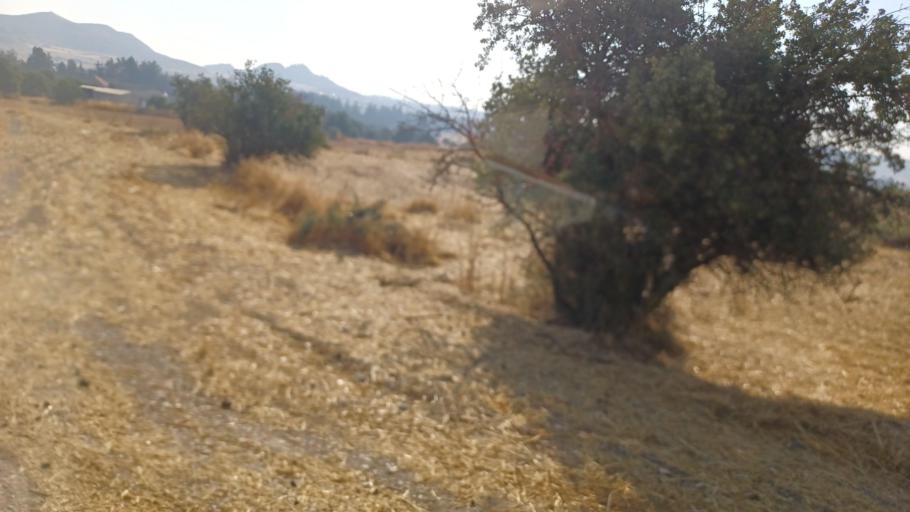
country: CY
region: Lefkosia
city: Lympia
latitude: 34.9945
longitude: 33.4327
